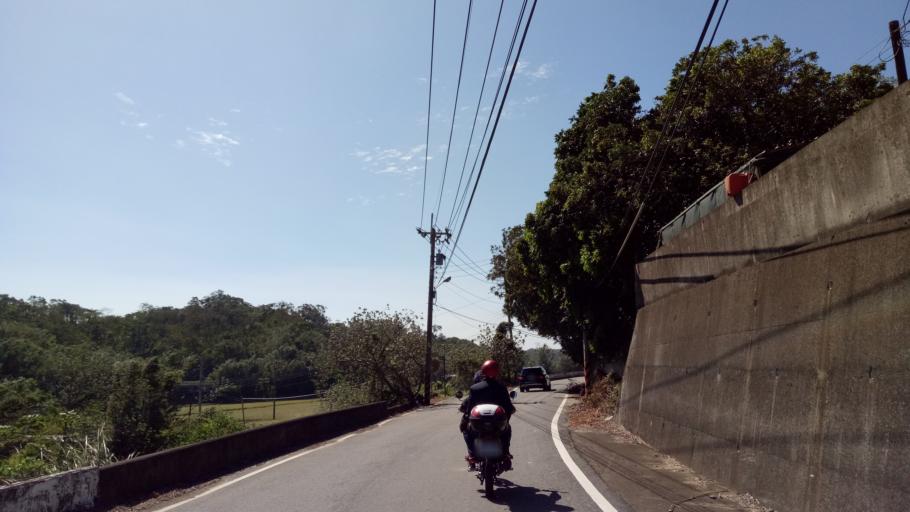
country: TW
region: Taiwan
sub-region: Hsinchu
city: Hsinchu
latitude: 24.7351
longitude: 120.9478
